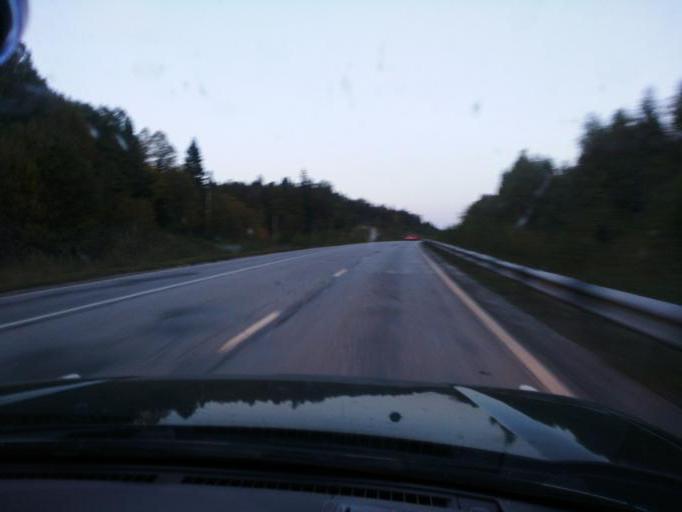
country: RU
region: Perm
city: Verkhnechusovskiye Gorodki
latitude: 58.2790
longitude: 56.9265
